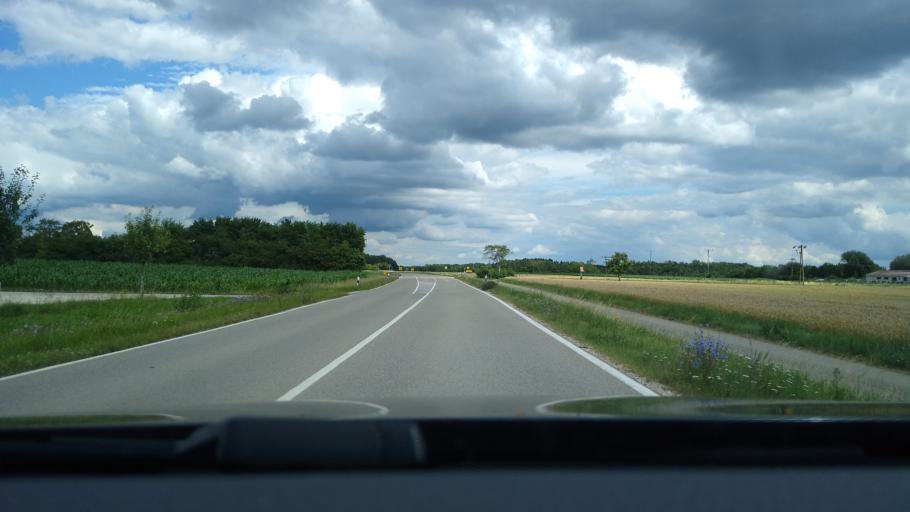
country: DE
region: Bavaria
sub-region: Regierungsbezirk Mittelfranken
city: Haundorf
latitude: 49.1541
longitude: 10.8107
